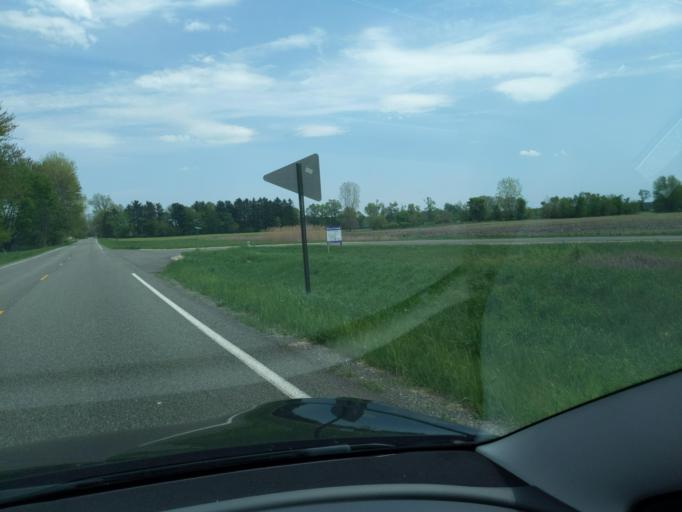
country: US
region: Michigan
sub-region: Ingham County
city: Stockbridge
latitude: 42.4899
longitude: -84.2902
